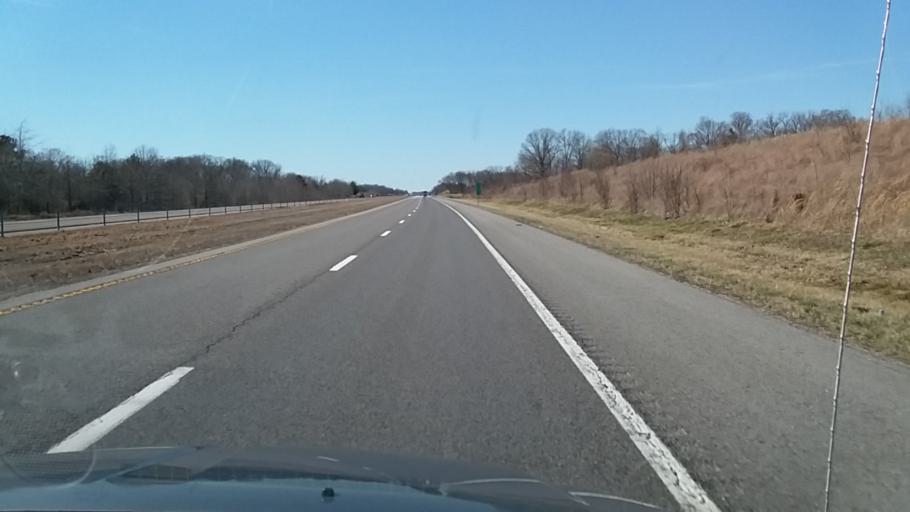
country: US
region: Missouri
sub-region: Perry County
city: Perryville
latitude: 37.5974
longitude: -89.7787
